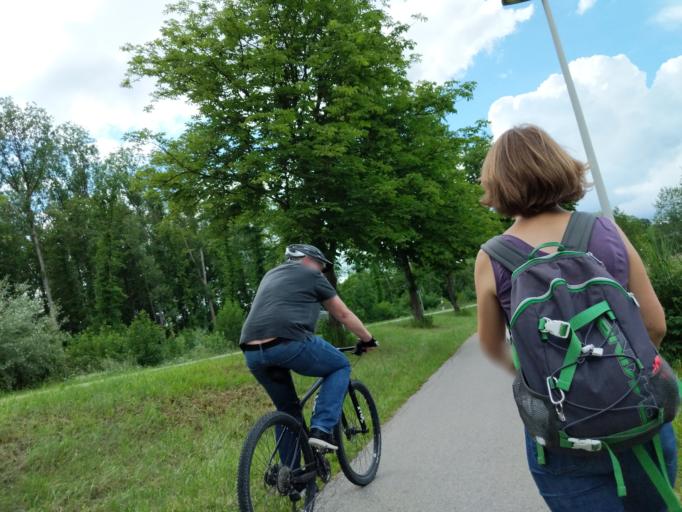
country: DE
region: Bavaria
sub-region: Upper Bavaria
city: Seefeld
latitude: 48.0348
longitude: 11.2019
